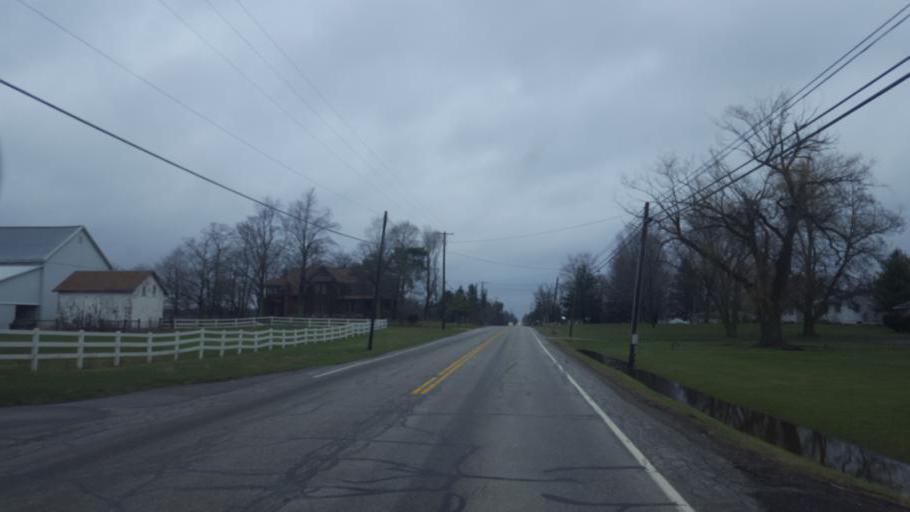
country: US
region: Ohio
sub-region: Medina County
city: Medina
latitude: 41.0833
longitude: -81.8642
